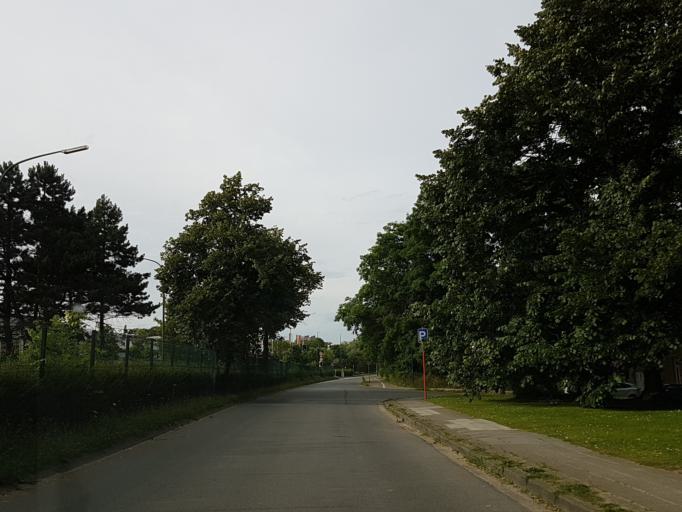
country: BE
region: Flanders
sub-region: Provincie Vlaams-Brabant
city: Kraainem
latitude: 50.8445
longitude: 4.4384
